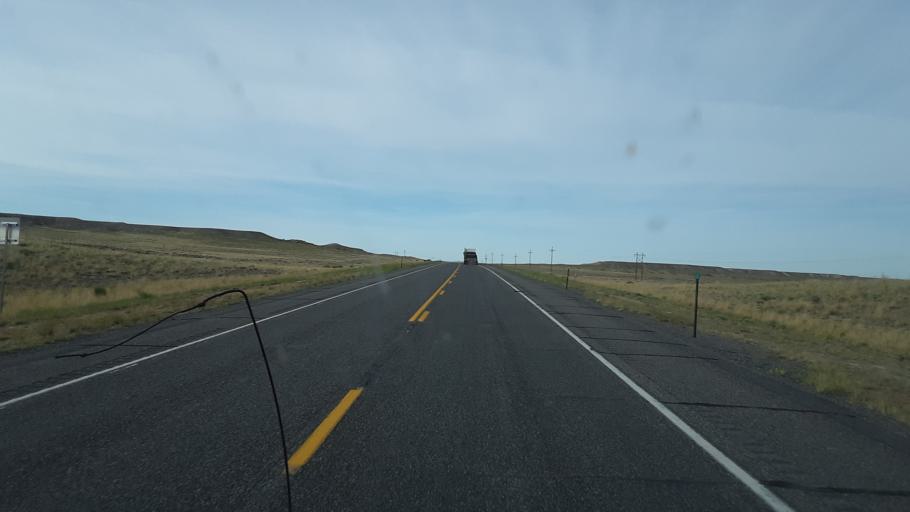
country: US
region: Wyoming
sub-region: Hot Springs County
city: Thermopolis
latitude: 43.3143
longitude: -108.1262
